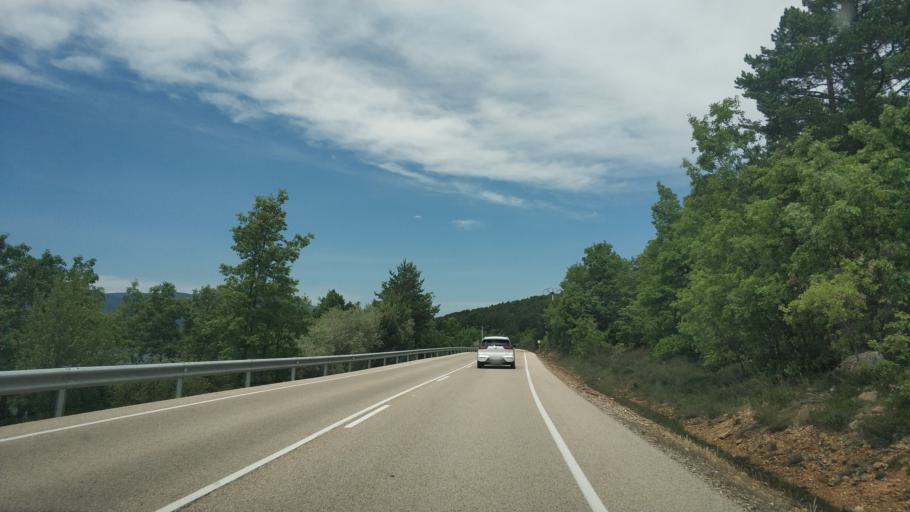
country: ES
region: Castille and Leon
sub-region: Provincia de Soria
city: Vinuesa
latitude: 41.8952
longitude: -2.7332
